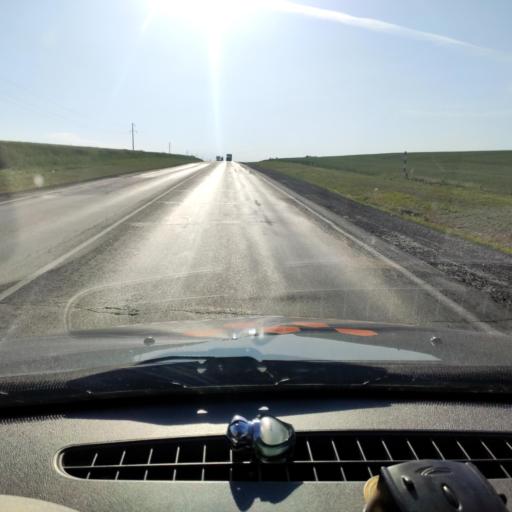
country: RU
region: Voronezj
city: Orlovo
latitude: 51.6825
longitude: 39.5662
